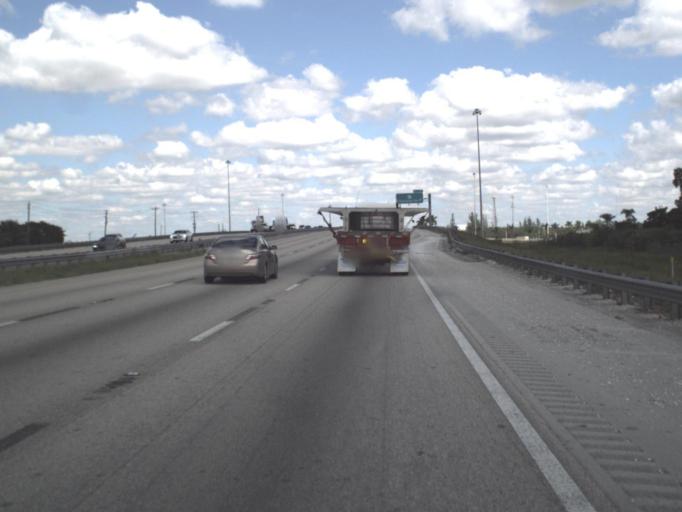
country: US
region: Florida
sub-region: Miami-Dade County
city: Palm Springs North
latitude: 25.8975
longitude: -80.3864
